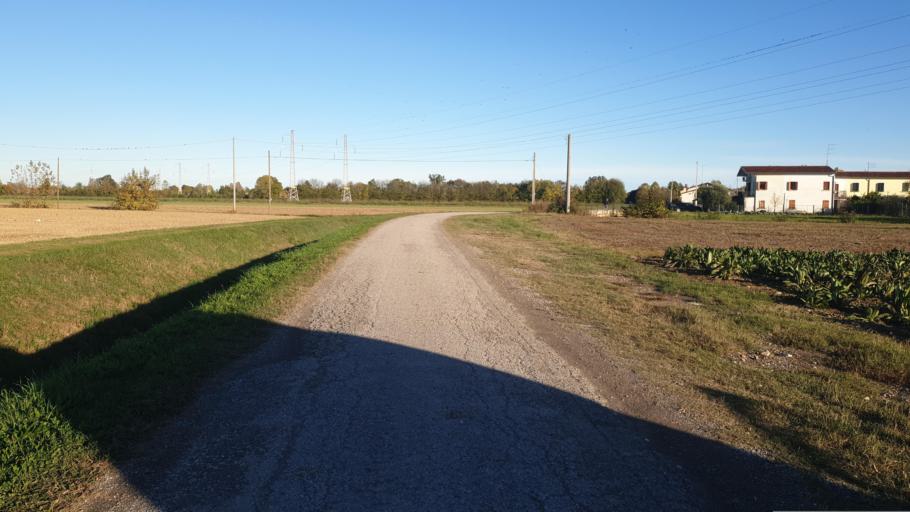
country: IT
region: Veneto
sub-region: Provincia di Venezia
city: Ballo
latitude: 45.4577
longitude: 12.0755
